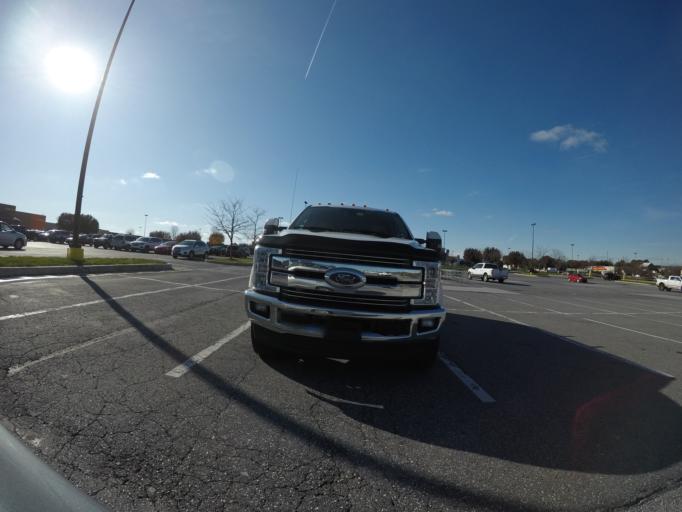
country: US
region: Pennsylvania
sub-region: Chester County
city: Parkesburg
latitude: 39.9812
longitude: -75.9339
